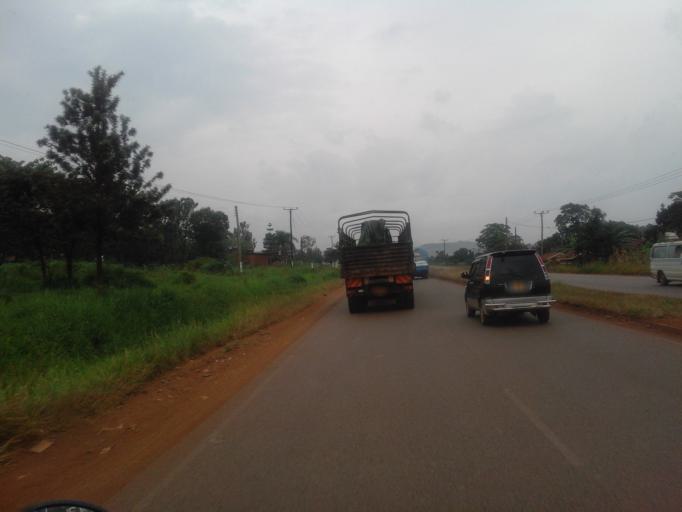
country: UG
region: Eastern Region
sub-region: Jinja District
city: Jinja
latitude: 0.4441
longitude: 33.2172
